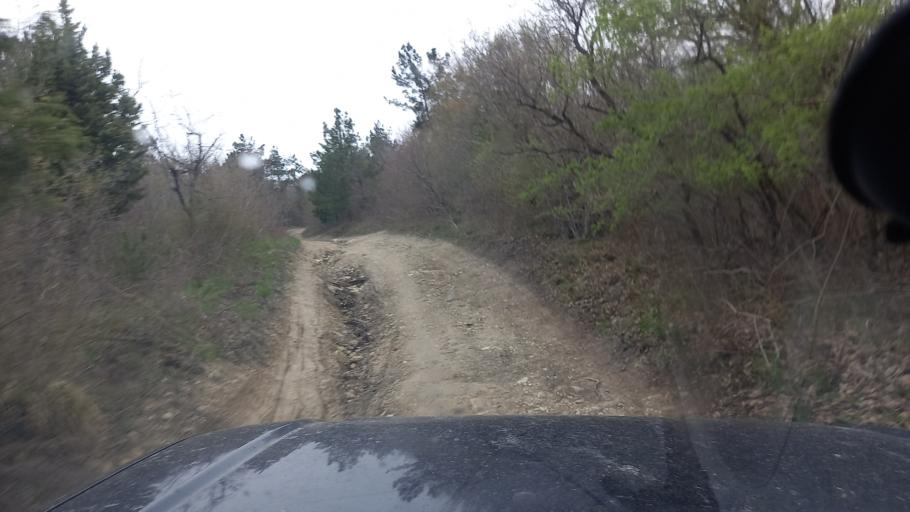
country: RU
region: Krasnodarskiy
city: Dzhubga
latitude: 44.3173
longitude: 38.6796
